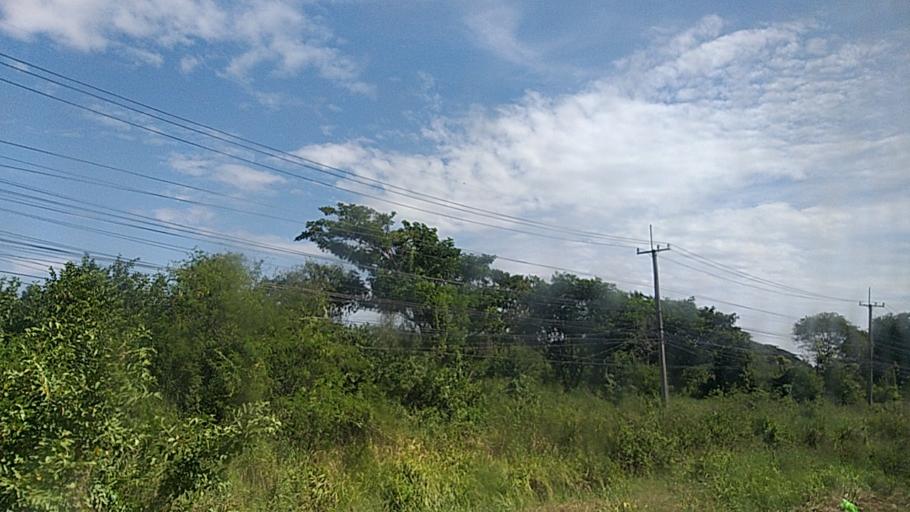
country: TH
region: Khon Kaen
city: Khon Kaen
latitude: 16.3872
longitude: 102.8211
